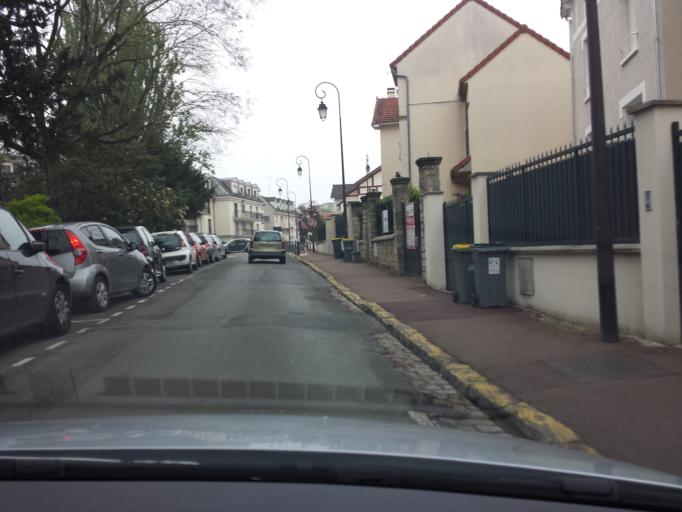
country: FR
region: Ile-de-France
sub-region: Departement des Hauts-de-Seine
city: Antony
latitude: 48.7512
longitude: 2.2968
